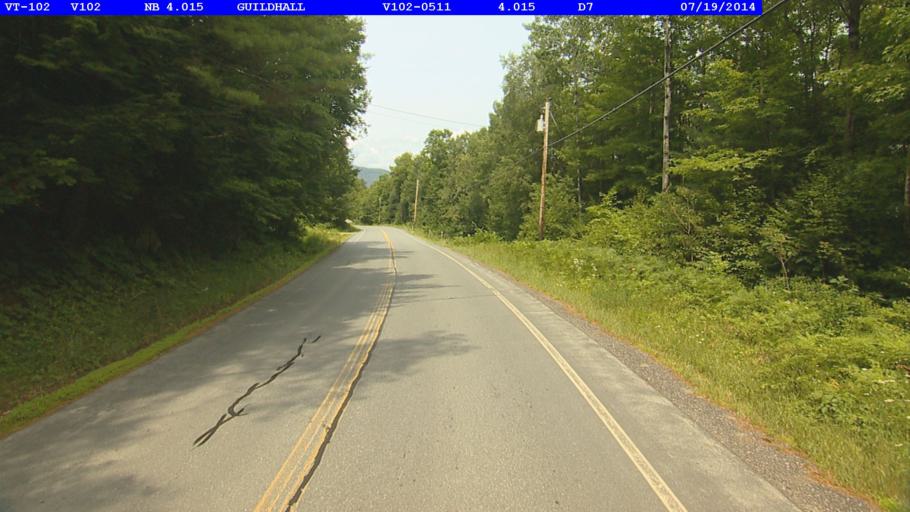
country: US
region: Vermont
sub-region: Essex County
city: Guildhall
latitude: 44.5479
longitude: -71.5893
